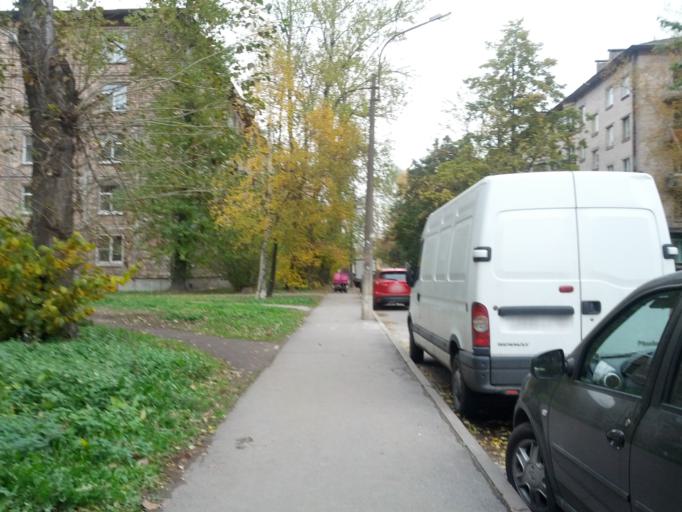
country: RU
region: St.-Petersburg
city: Obukhovo
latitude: 59.8936
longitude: 30.4210
